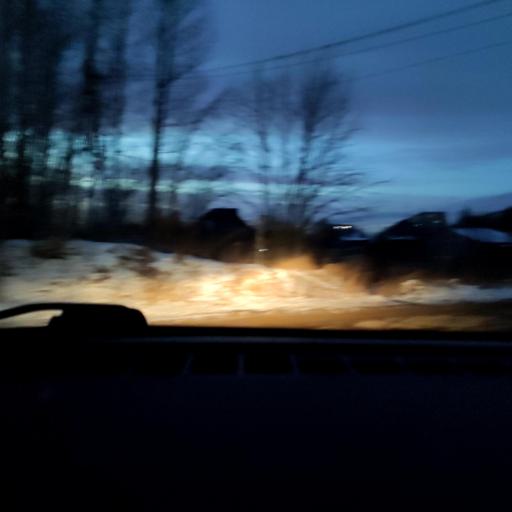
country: RU
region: Perm
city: Kondratovo
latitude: 57.9571
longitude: 56.1524
